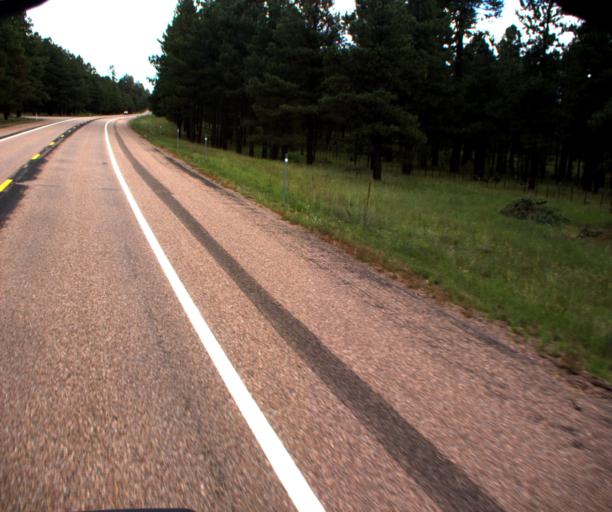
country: US
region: Arizona
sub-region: Navajo County
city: Pinetop-Lakeside
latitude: 34.0416
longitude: -109.6766
